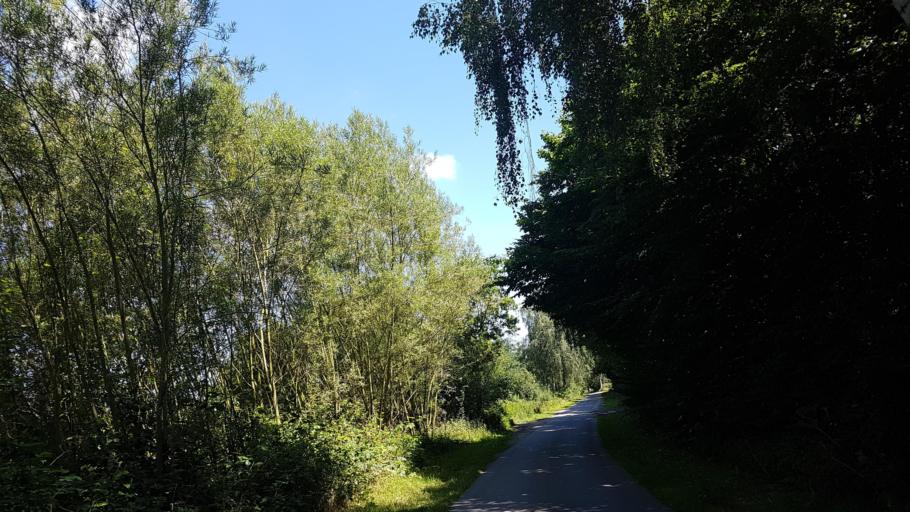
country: DE
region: Lower Saxony
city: Rullstorf
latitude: 53.2843
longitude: 10.5210
